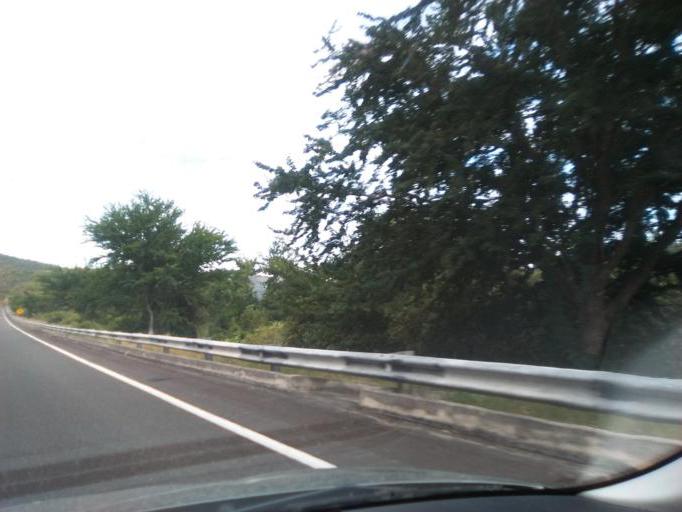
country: MX
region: Guerrero
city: Huitziltepec
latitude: 17.7613
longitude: -99.4838
